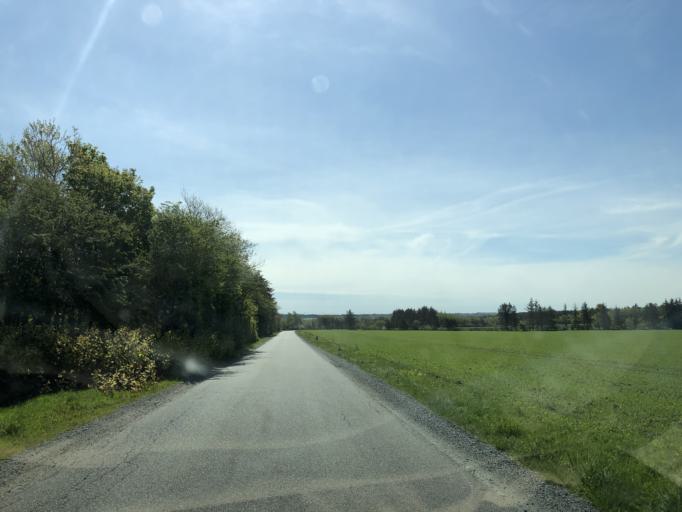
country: DK
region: Central Jutland
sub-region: Ringkobing-Skjern Kommune
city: Videbaek
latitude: 56.1689
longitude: 8.5326
